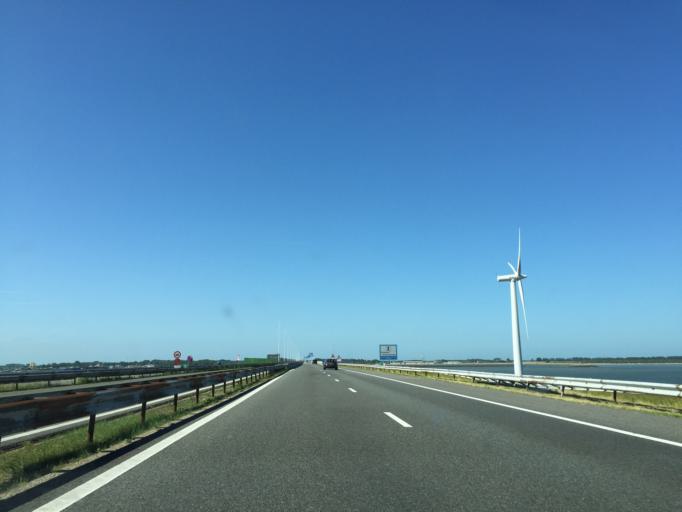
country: NL
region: South Holland
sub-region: Gemeente Hellevoetsluis
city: Nieuw-Helvoet
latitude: 51.8379
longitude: 4.0567
